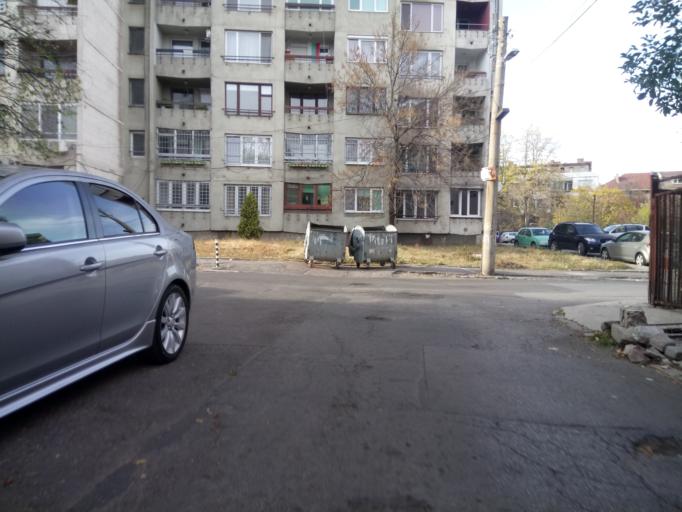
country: BG
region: Sofia-Capital
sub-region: Stolichna Obshtina
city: Sofia
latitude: 42.6826
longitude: 23.3557
